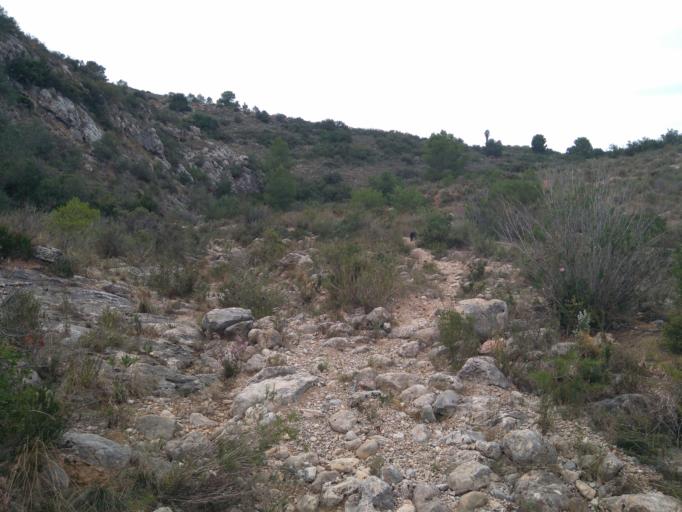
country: ES
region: Valencia
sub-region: Provincia de Valencia
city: Benimodo
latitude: 39.1956
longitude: -0.5743
